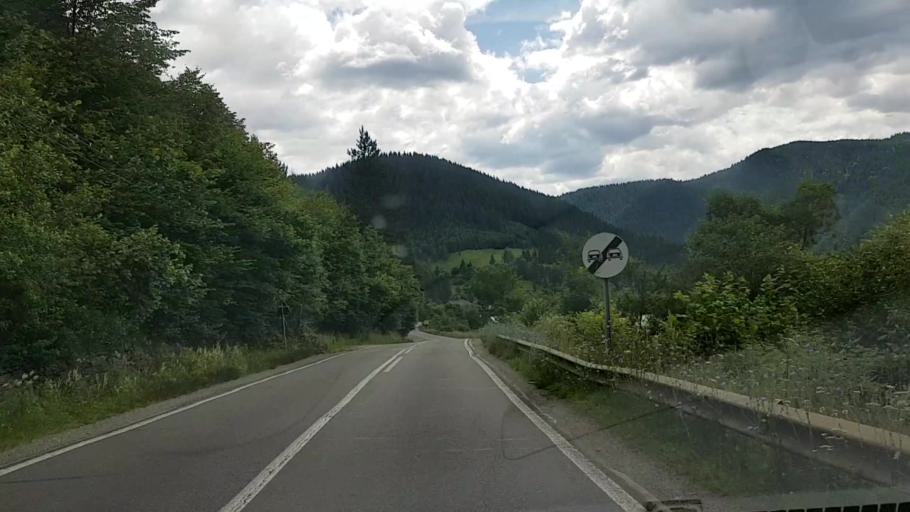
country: RO
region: Suceava
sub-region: Comuna Brosteni
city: Brosteni
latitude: 47.2342
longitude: 25.7434
